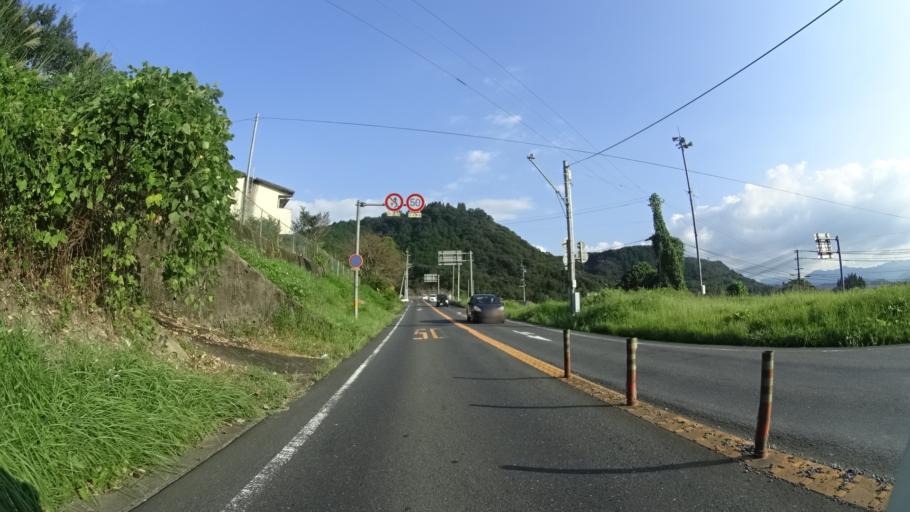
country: JP
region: Oita
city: Bungo-Takada-shi
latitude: 33.4469
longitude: 131.3327
